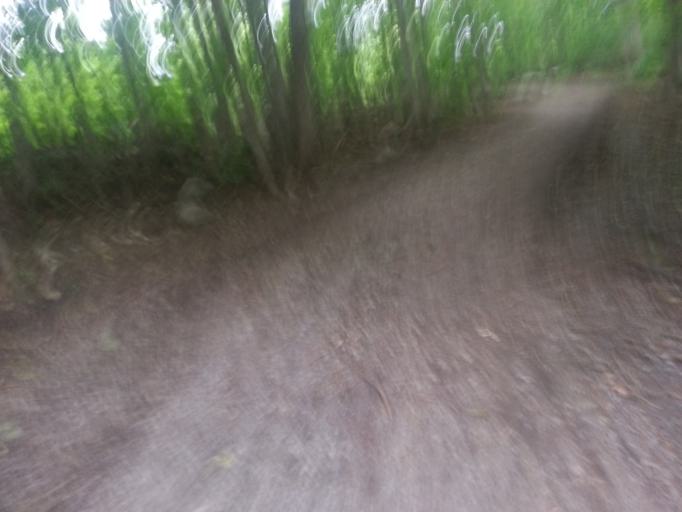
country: CA
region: Ontario
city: Bells Corners
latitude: 45.3262
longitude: -75.9208
